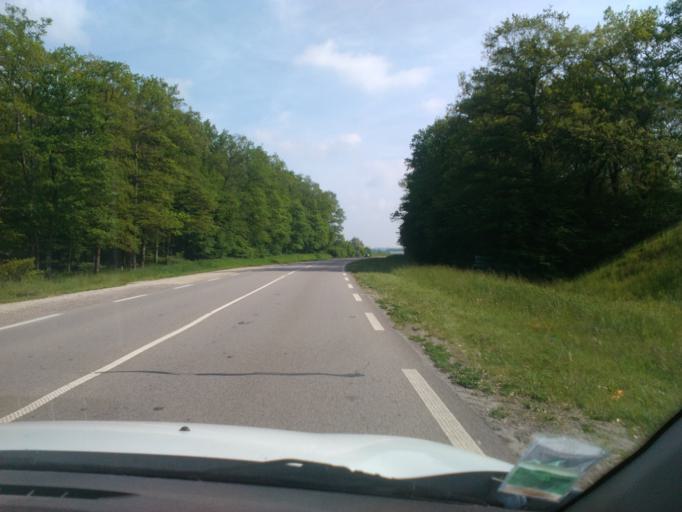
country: FR
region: Lorraine
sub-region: Departement des Vosges
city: Golbey
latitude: 48.2119
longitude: 6.4198
